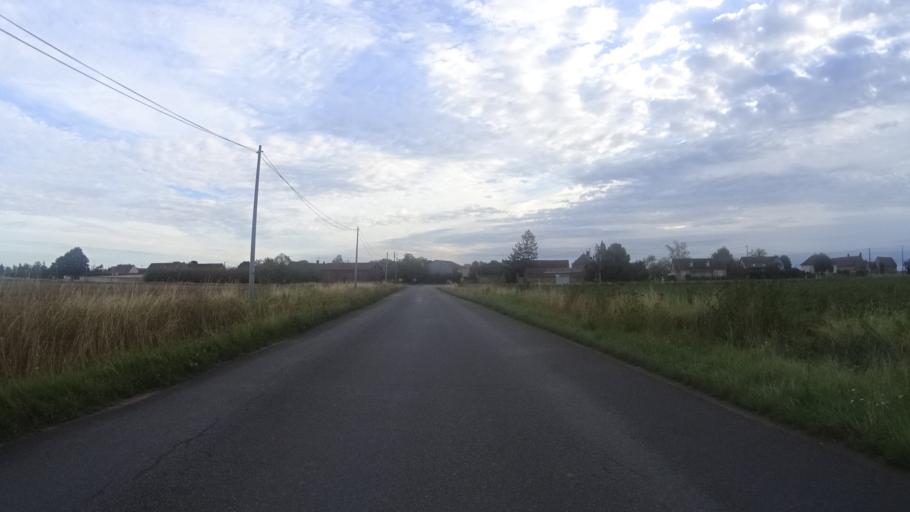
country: FR
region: Centre
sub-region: Departement du Loiret
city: Saint-Benoit-sur-Loire
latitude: 47.7995
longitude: 2.3121
